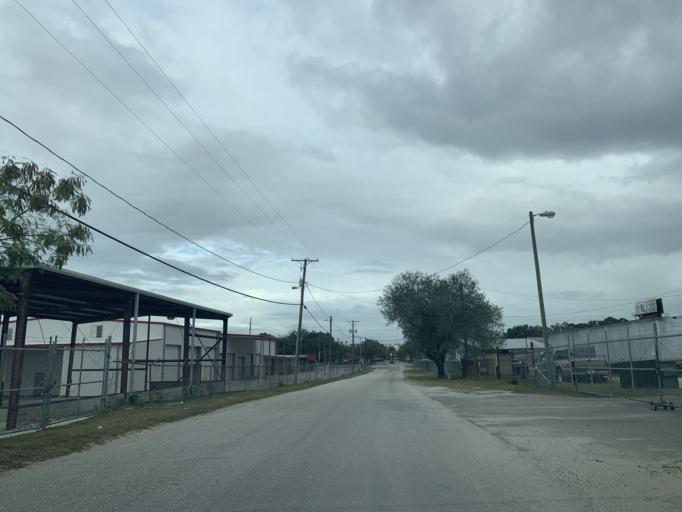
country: US
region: Florida
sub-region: Hillsborough County
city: East Lake-Orient Park
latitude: 27.9925
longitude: -82.3956
